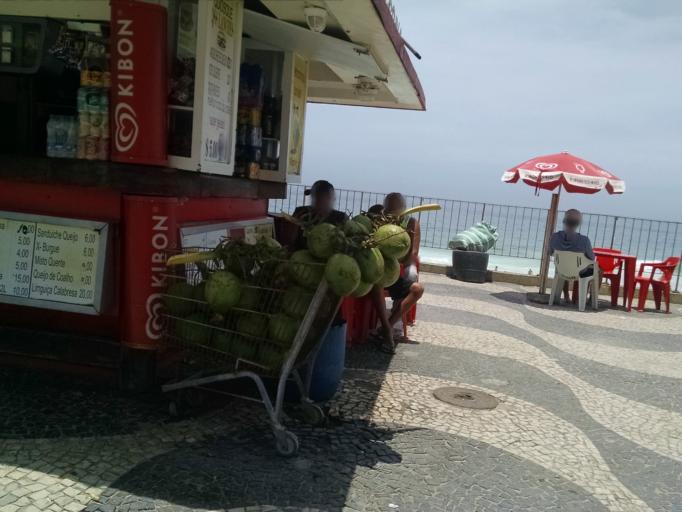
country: BR
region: Rio de Janeiro
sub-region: Rio De Janeiro
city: Rio de Janeiro
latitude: -22.9986
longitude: -43.2566
